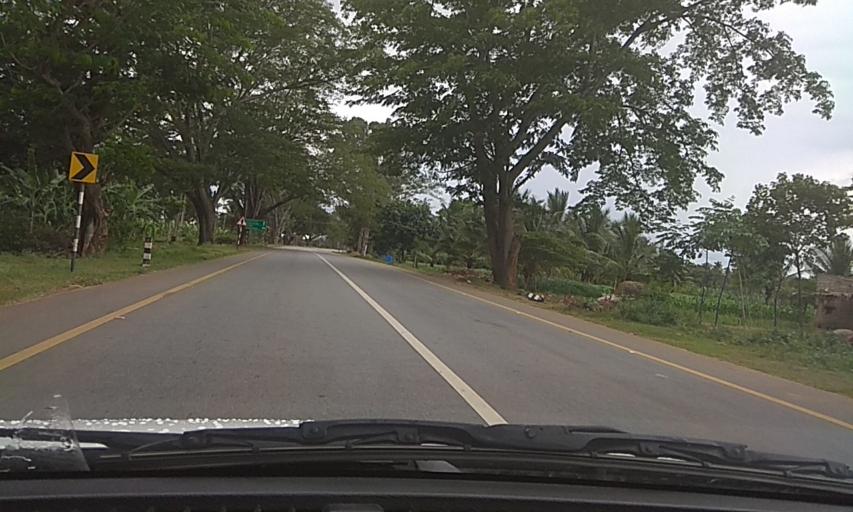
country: IN
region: Karnataka
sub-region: Tumkur
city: Kunigal
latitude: 12.9195
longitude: 77.0323
